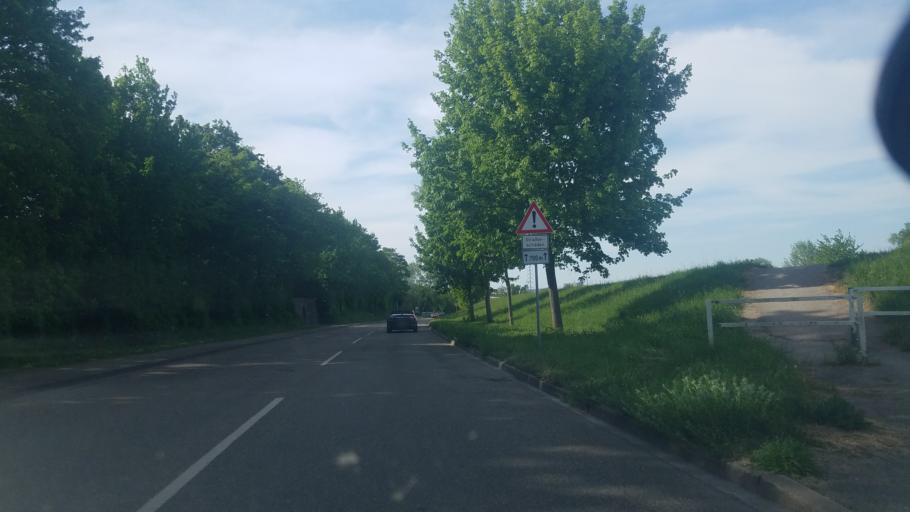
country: DE
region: Baden-Wuerttemberg
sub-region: Freiburg Region
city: Kehl
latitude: 48.5733
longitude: 7.8248
